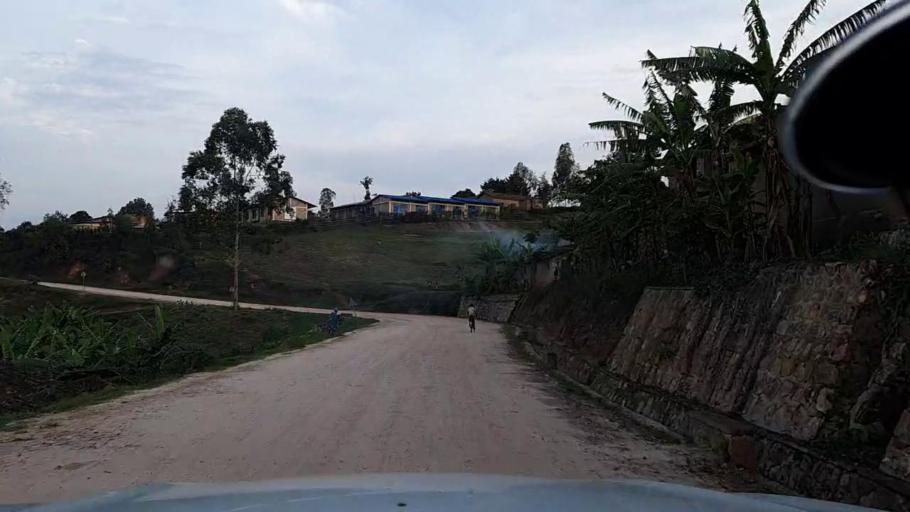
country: RW
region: Southern Province
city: Nyanza
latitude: -2.2225
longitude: 29.6484
